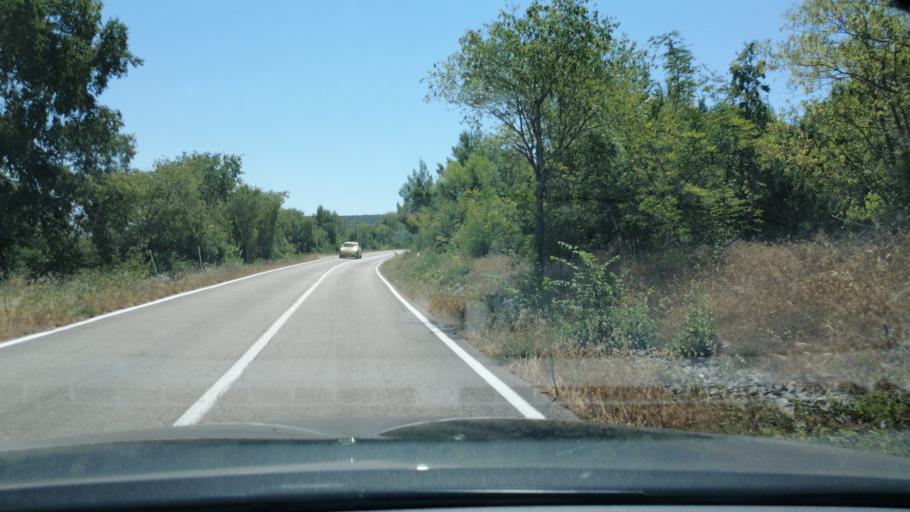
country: HR
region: Sibensko-Kniniska
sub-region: Grad Sibenik
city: Pirovac
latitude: 43.8654
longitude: 15.6881
